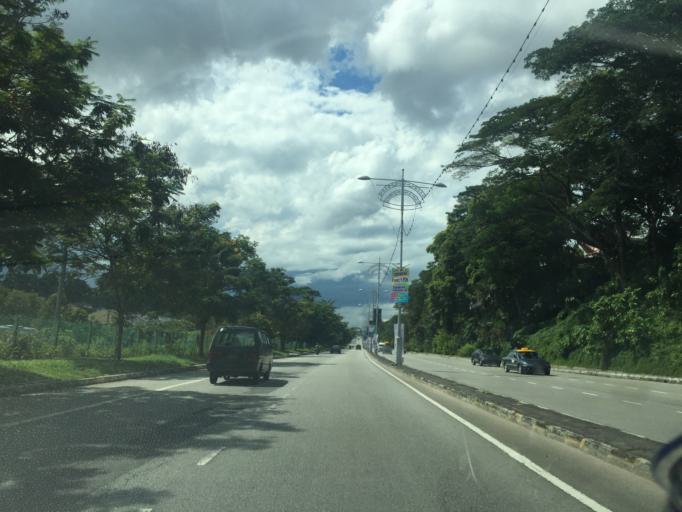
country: MY
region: Negeri Sembilan
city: Seremban
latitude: 2.7216
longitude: 101.9347
